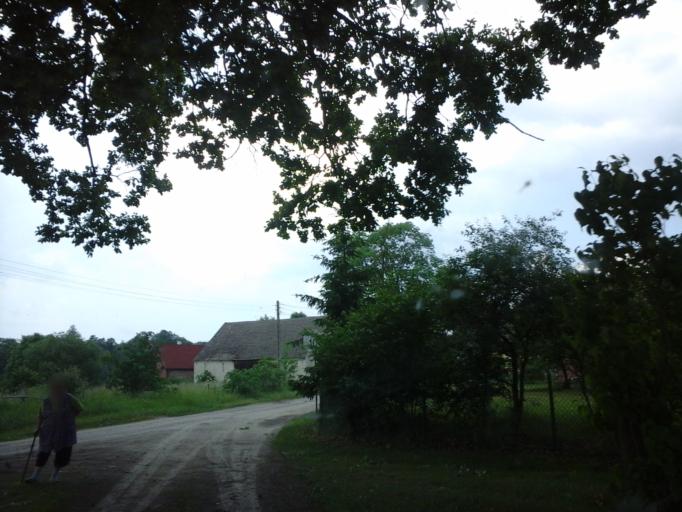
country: PL
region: West Pomeranian Voivodeship
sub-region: Powiat choszczenski
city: Drawno
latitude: 53.2005
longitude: 15.8430
